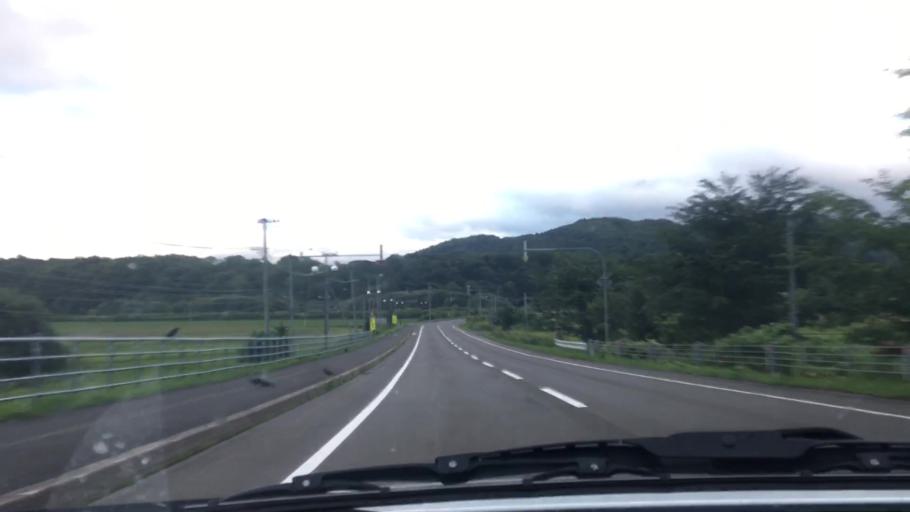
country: JP
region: Hokkaido
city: Shimo-furano
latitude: 42.9865
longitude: 142.3987
